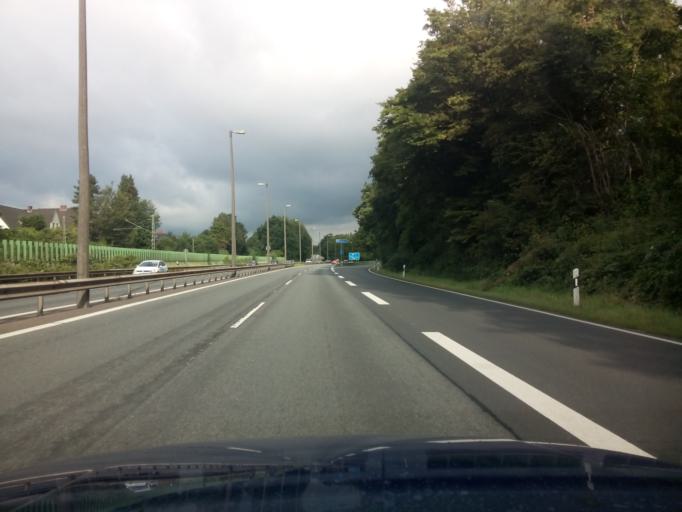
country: DE
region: Lower Saxony
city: Lemwerder
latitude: 53.1727
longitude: 8.6587
